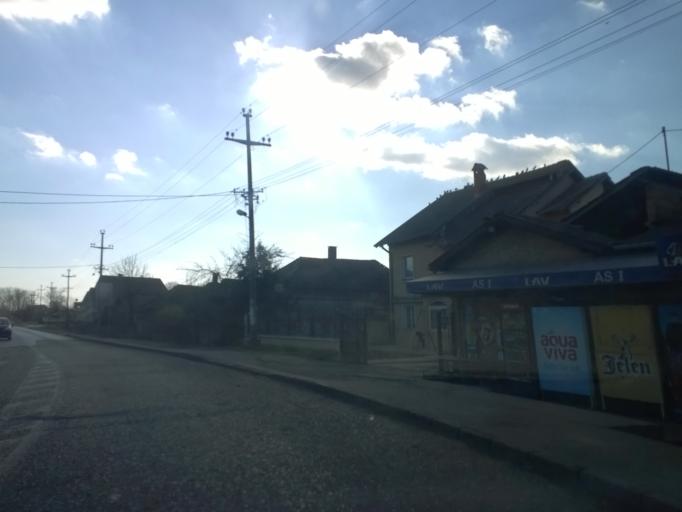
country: RS
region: Central Serbia
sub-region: Podunavski Okrug
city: Smederevo
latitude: 44.5925
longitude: 20.9705
